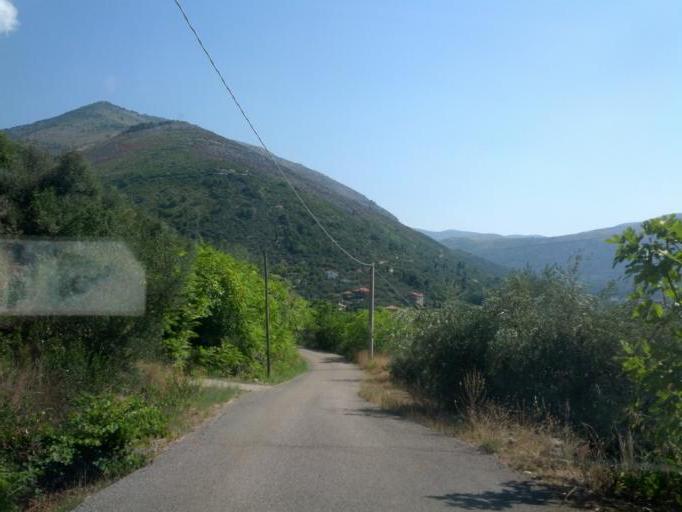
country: IT
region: Latium
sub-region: Provincia di Latina
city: Monte San Biagio
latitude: 41.3801
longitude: 13.3851
